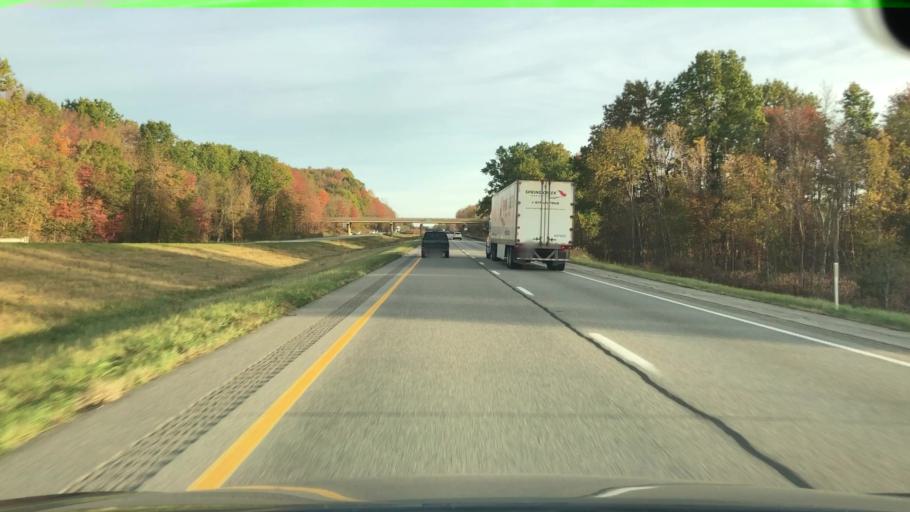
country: US
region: Pennsylvania
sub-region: Mercer County
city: Stoneboro
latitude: 41.2925
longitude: -80.1578
